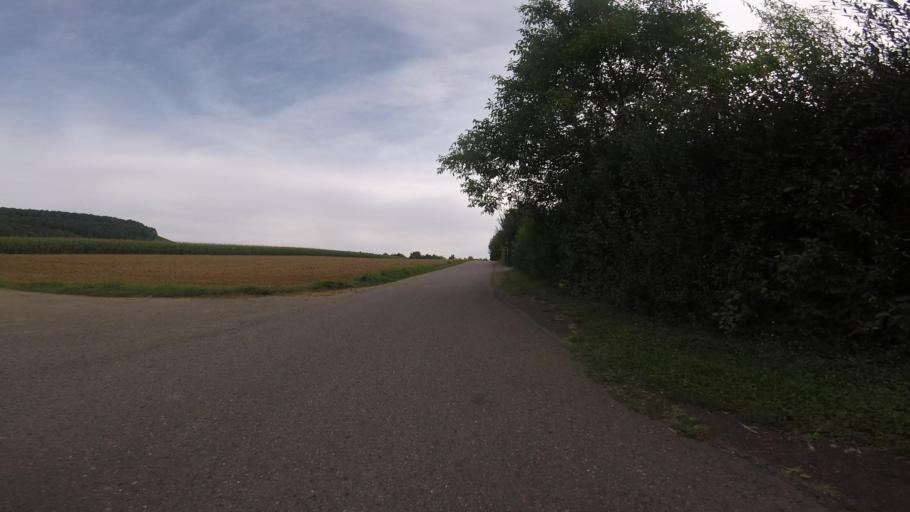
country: DE
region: Baden-Wuerttemberg
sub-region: Regierungsbezirk Stuttgart
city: Grossbottwar
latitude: 49.0024
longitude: 9.3052
